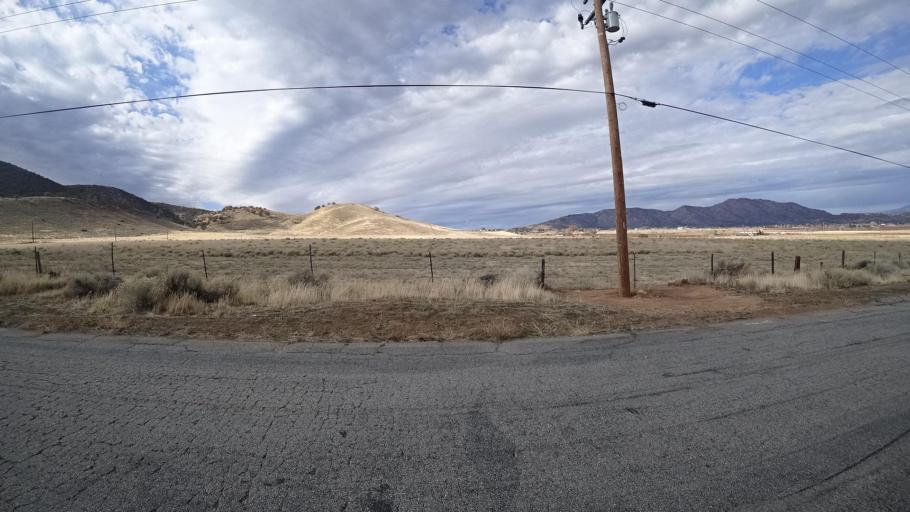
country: US
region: California
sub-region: Kern County
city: Tehachapi
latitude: 35.1054
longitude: -118.4679
